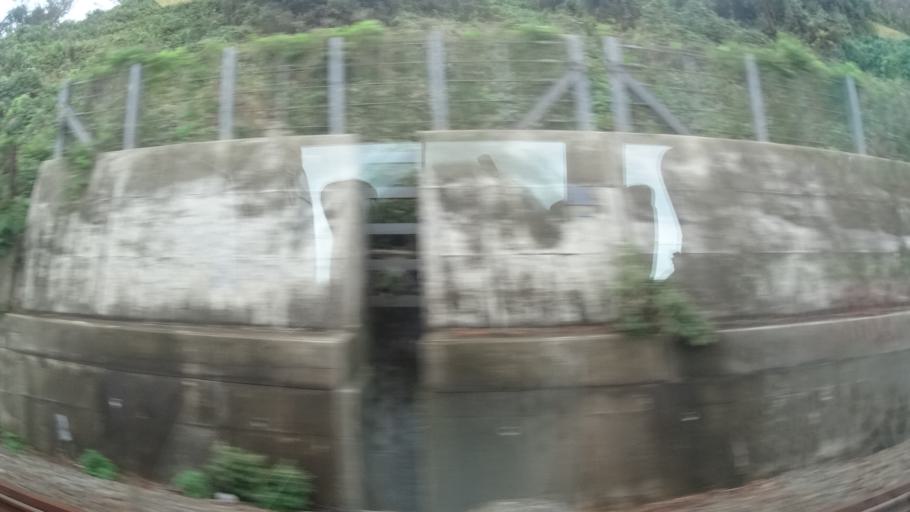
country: JP
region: Yamagata
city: Tsuruoka
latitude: 38.6503
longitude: 139.5997
